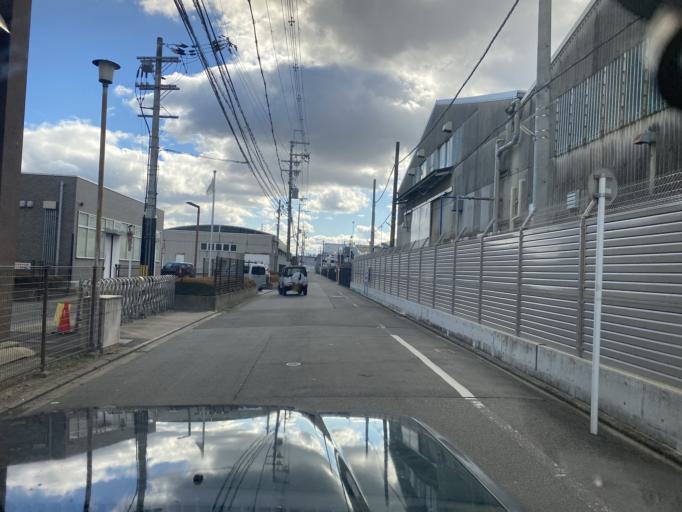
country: JP
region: Kyoto
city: Muko
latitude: 34.9660
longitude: 135.7557
